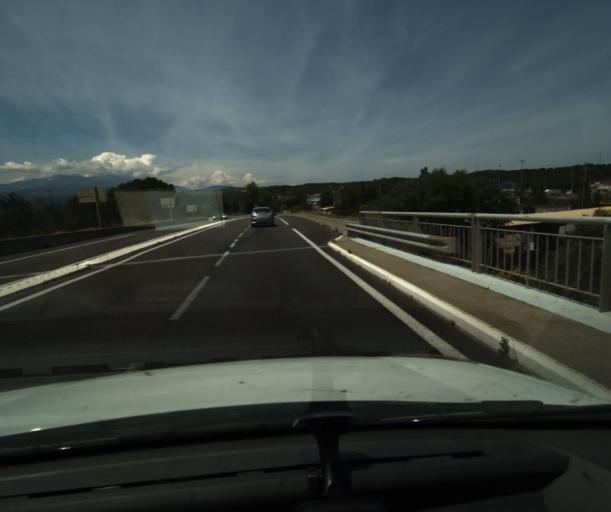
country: FR
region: Languedoc-Roussillon
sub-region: Departement des Pyrenees-Orientales
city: el Volo
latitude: 42.5210
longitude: 2.8189
